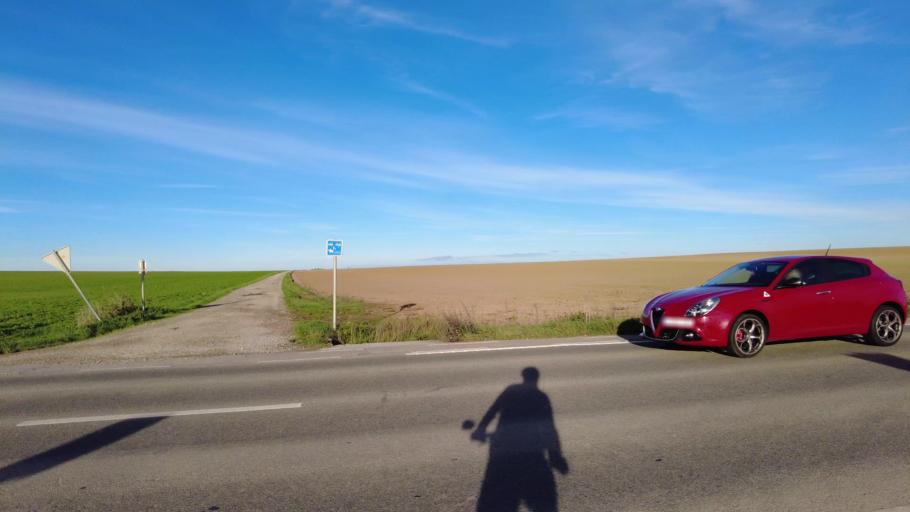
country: BE
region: Wallonia
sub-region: Province du Brabant Wallon
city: Jodoigne
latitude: 50.7111
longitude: 4.9018
